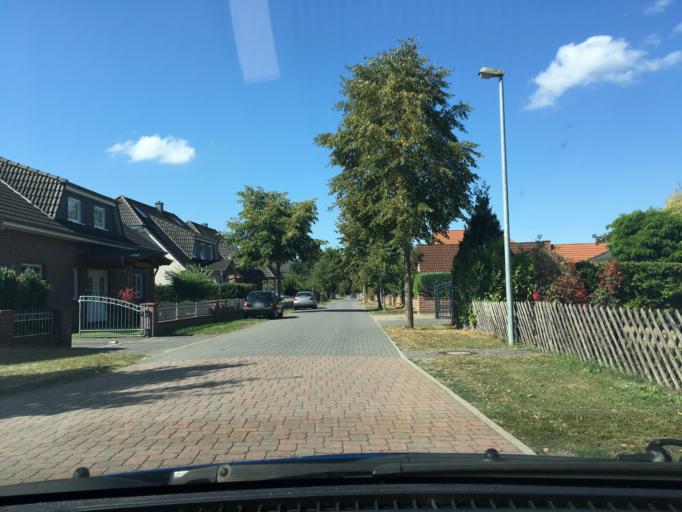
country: DE
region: Lower Saxony
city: Winsen (Aller)
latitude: 52.6705
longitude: 9.9084
